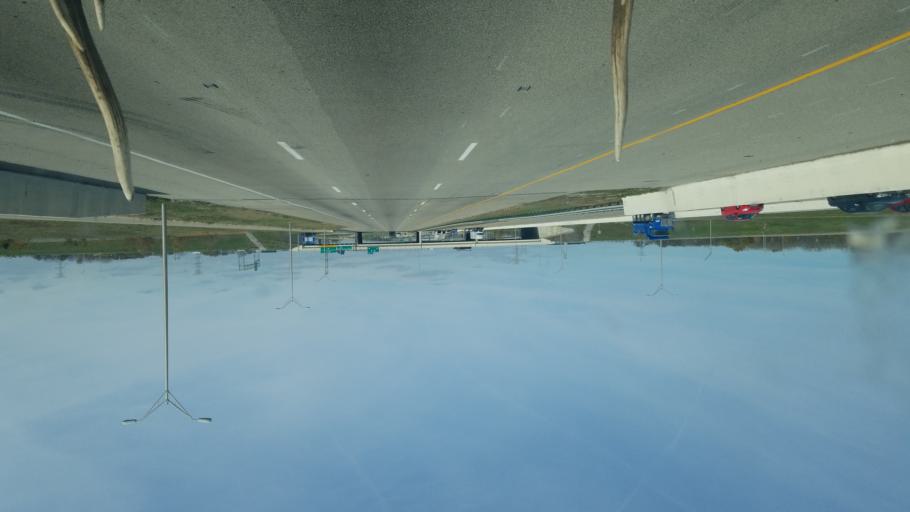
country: US
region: Indiana
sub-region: Hendricks County
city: Plainfield
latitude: 39.6833
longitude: -86.3331
